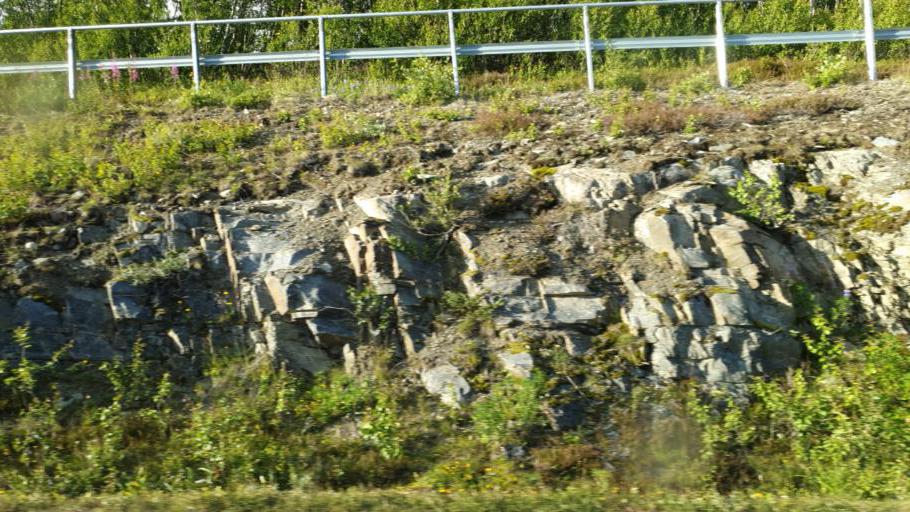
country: NO
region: Oppland
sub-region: Vestre Slidre
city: Slidre
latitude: 61.2507
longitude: 8.8847
